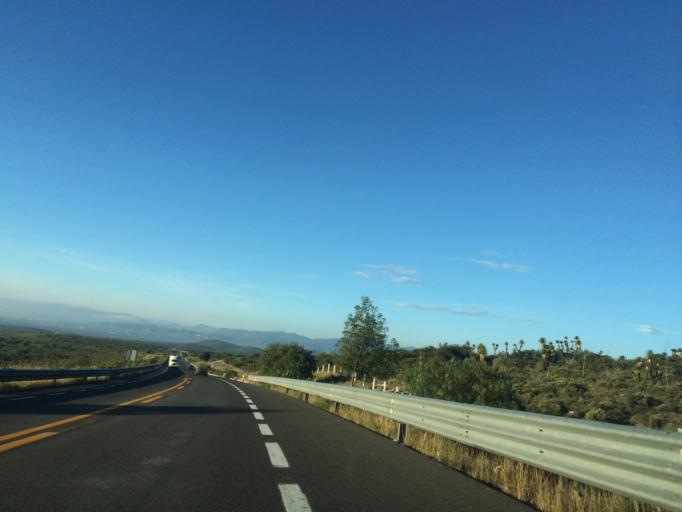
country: MX
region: Puebla
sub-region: Tehuacan
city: Magdalena Cuayucatepec
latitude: 18.6133
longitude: -97.4759
